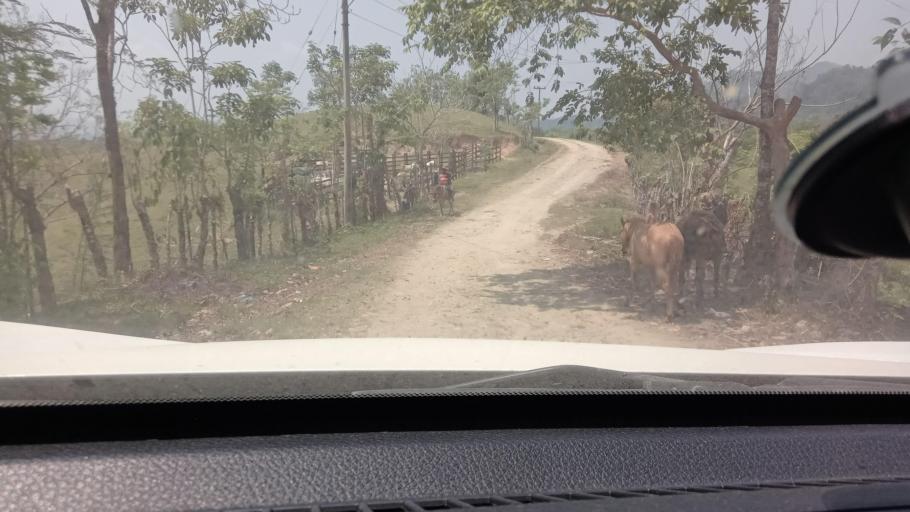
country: MX
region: Tabasco
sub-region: Huimanguillo
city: Francisco Rueda
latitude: 17.4819
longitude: -93.9440
